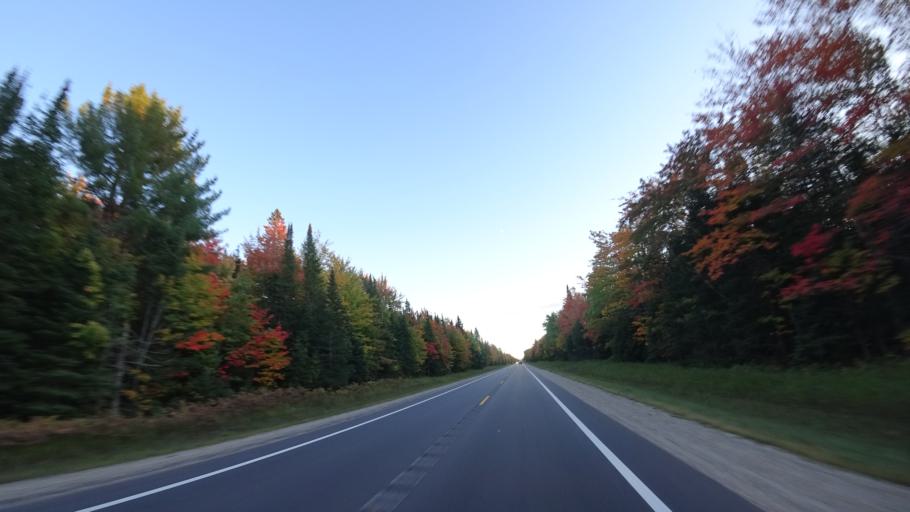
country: US
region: Michigan
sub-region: Mackinac County
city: Saint Ignace
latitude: 46.2660
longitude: -85.0094
